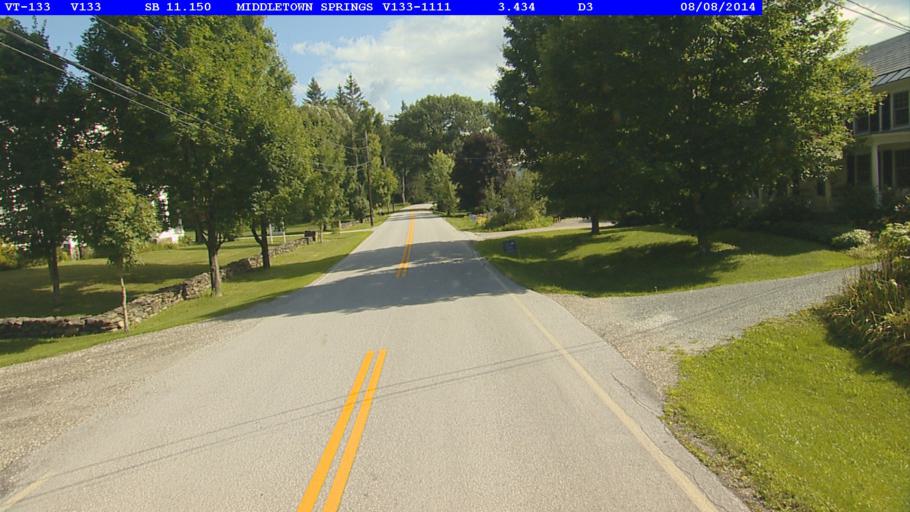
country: US
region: Vermont
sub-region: Rutland County
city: Poultney
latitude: 43.4823
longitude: -73.1184
